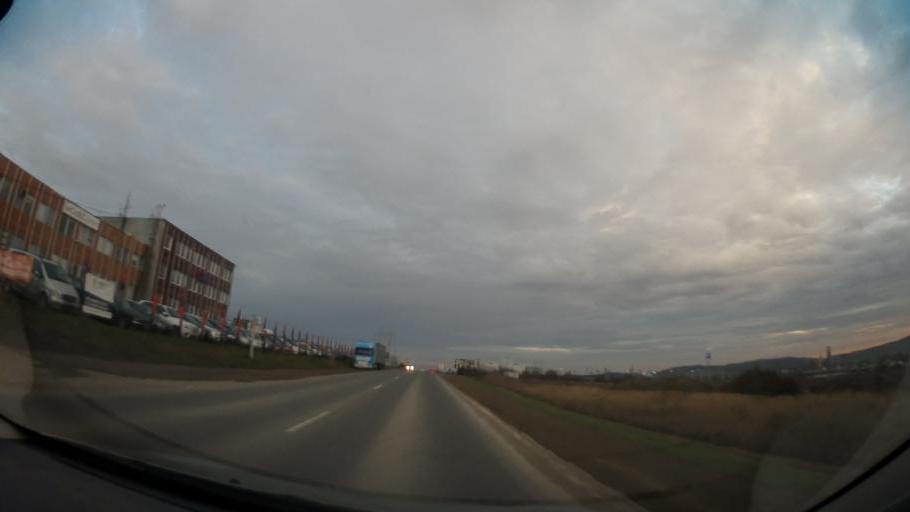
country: CZ
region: South Moravian
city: Troubsko
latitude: 49.1780
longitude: 16.5004
